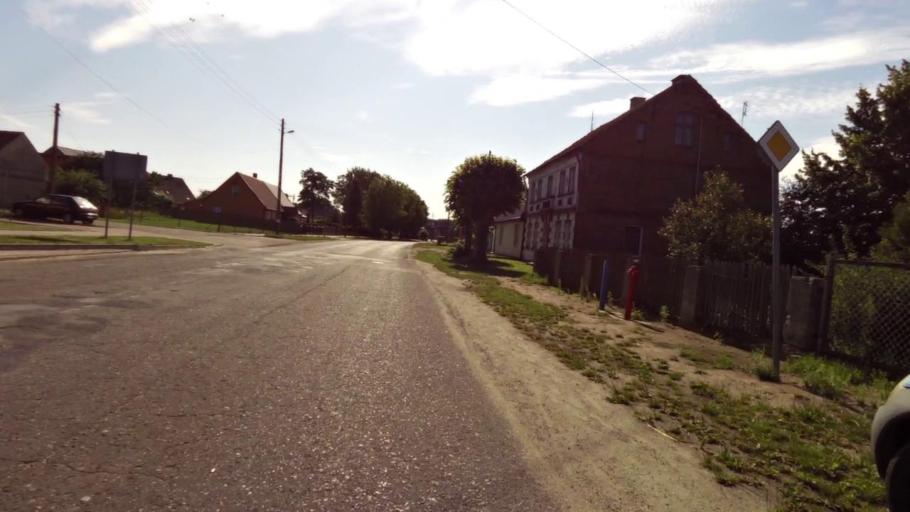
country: PL
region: West Pomeranian Voivodeship
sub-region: Powiat stargardzki
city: Marianowo
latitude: 53.3824
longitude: 15.2685
